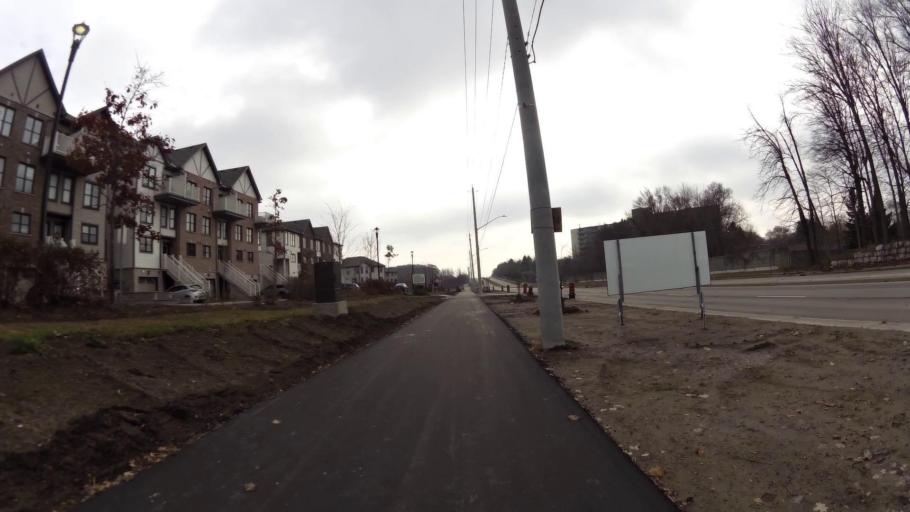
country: CA
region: Ontario
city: Kitchener
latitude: 43.4168
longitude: -80.4689
